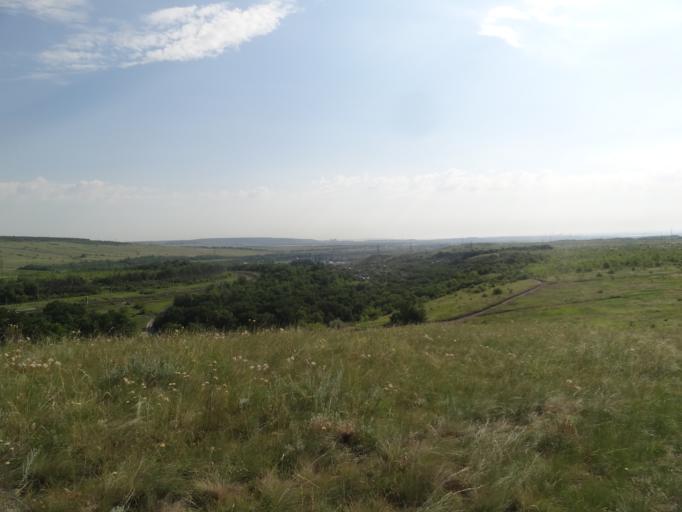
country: RU
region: Saratov
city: Sokolovyy
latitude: 51.4385
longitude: 45.7953
